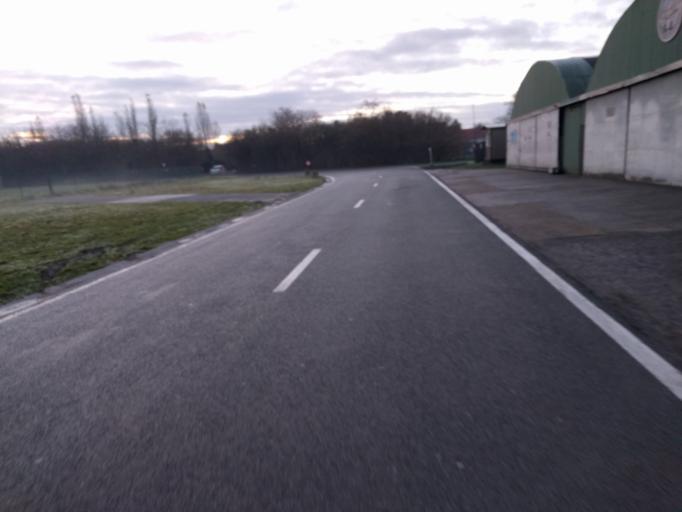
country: BE
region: Flanders
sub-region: Provincie West-Vlaanderen
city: Wevelgem
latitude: 50.8137
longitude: 3.1933
